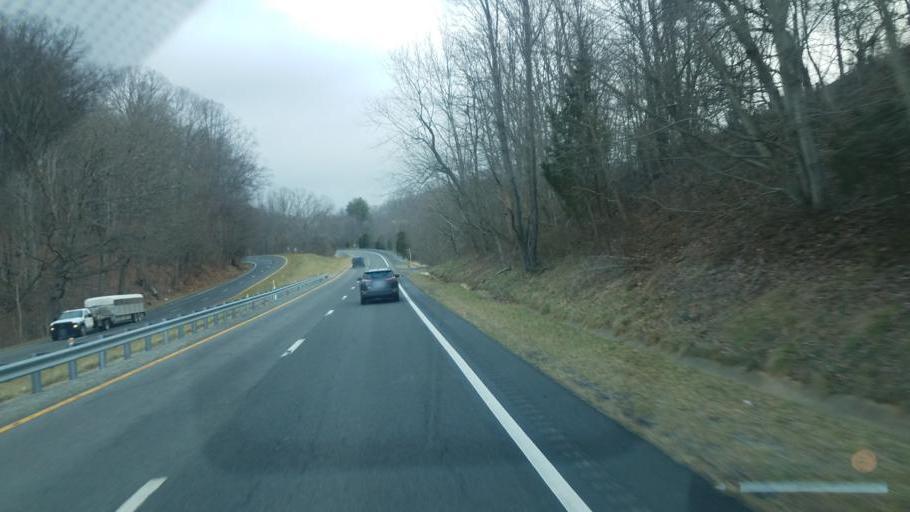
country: US
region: Virginia
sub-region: Giles County
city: Pearisburg
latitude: 37.2862
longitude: -80.7429
